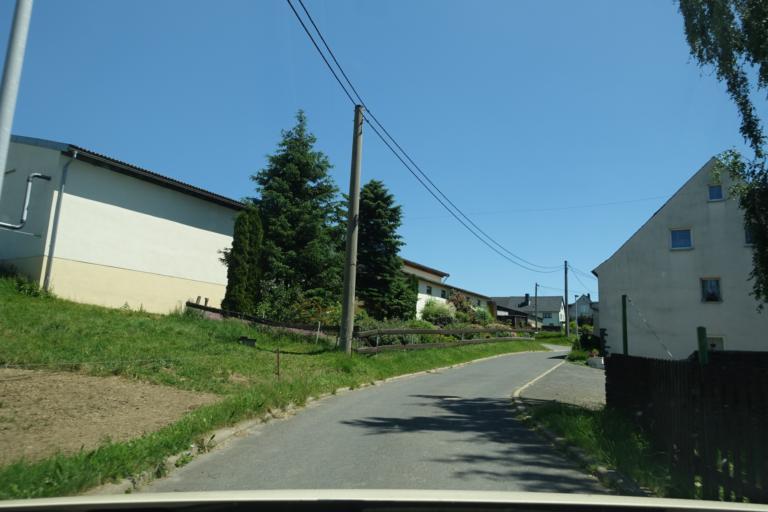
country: DE
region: Saxony
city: Leubsdorf
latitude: 50.8010
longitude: 13.1779
